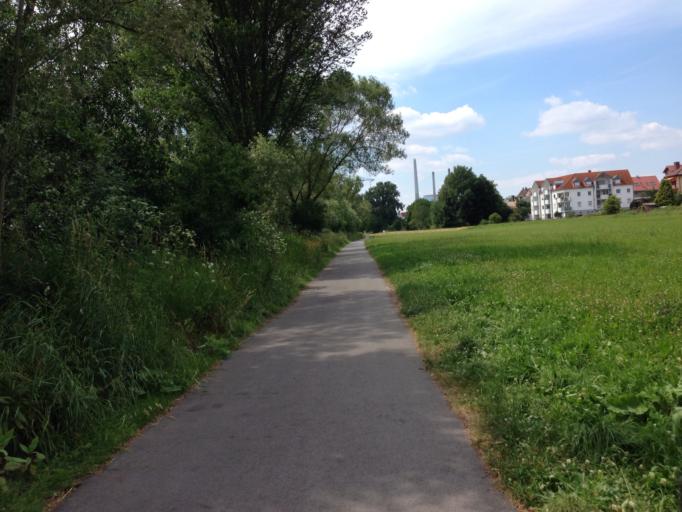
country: DE
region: Hesse
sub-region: Regierungsbezirk Darmstadt
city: Grosskrotzenburg
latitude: 50.0787
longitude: 8.9792
